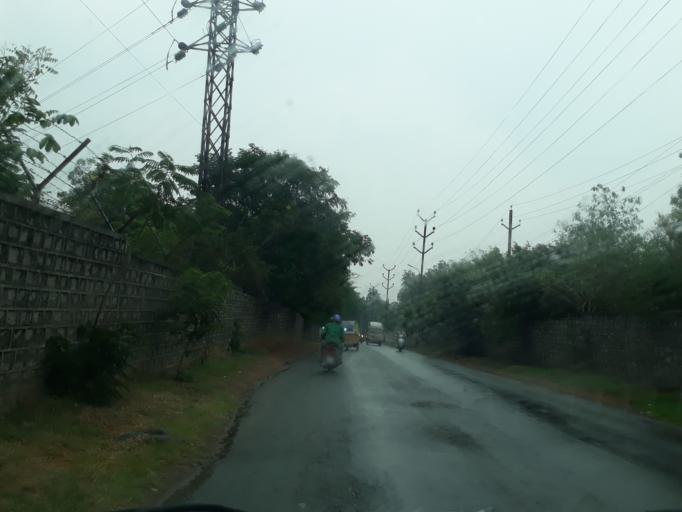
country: IN
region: Telangana
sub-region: Hyderabad
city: Malkajgiri
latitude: 17.4675
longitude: 78.5040
